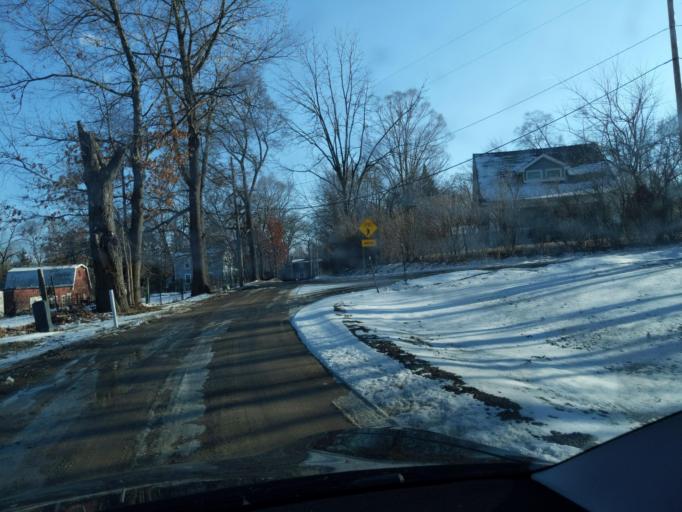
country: US
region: Michigan
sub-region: Ingham County
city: Stockbridge
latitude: 42.4616
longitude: -84.0797
